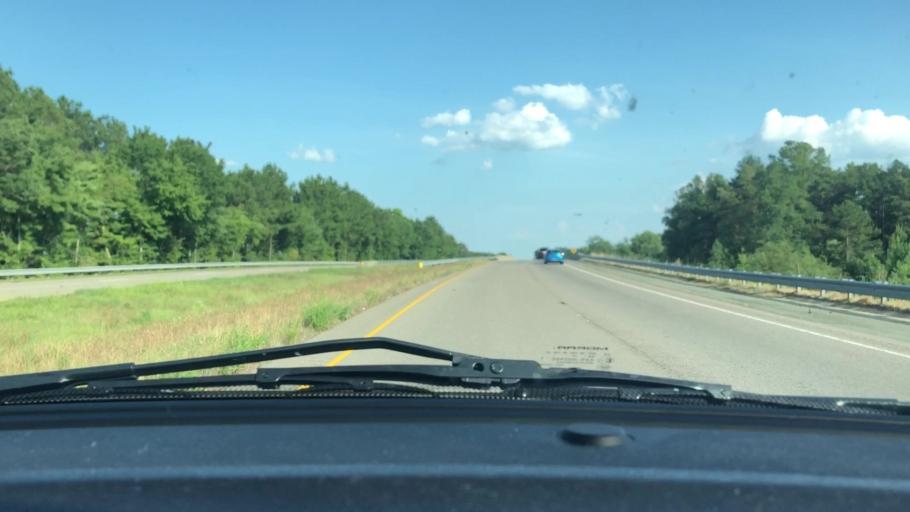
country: US
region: North Carolina
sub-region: Chatham County
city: Farmville
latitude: 35.5670
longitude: -79.2995
